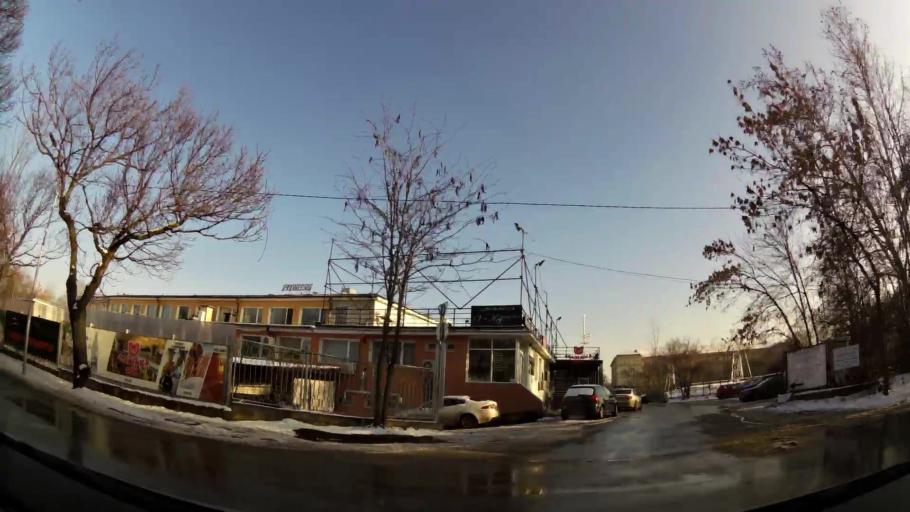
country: BG
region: Sofia-Capital
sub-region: Stolichna Obshtina
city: Sofia
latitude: 42.6759
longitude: 23.3645
